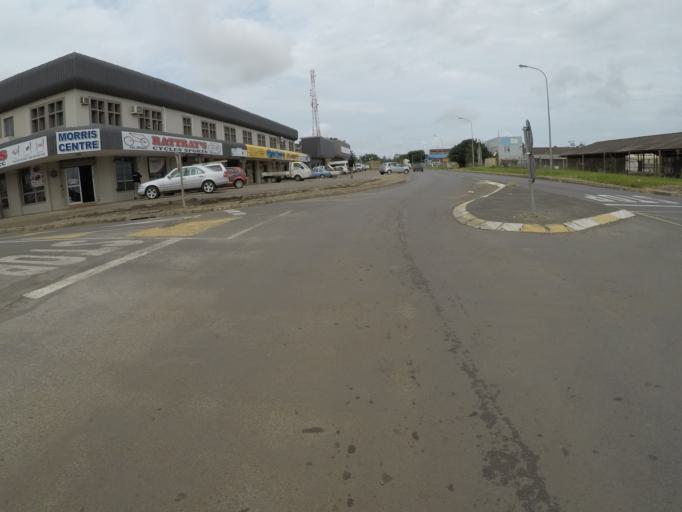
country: ZA
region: KwaZulu-Natal
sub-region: uThungulu District Municipality
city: Empangeni
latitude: -28.7687
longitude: 31.9045
